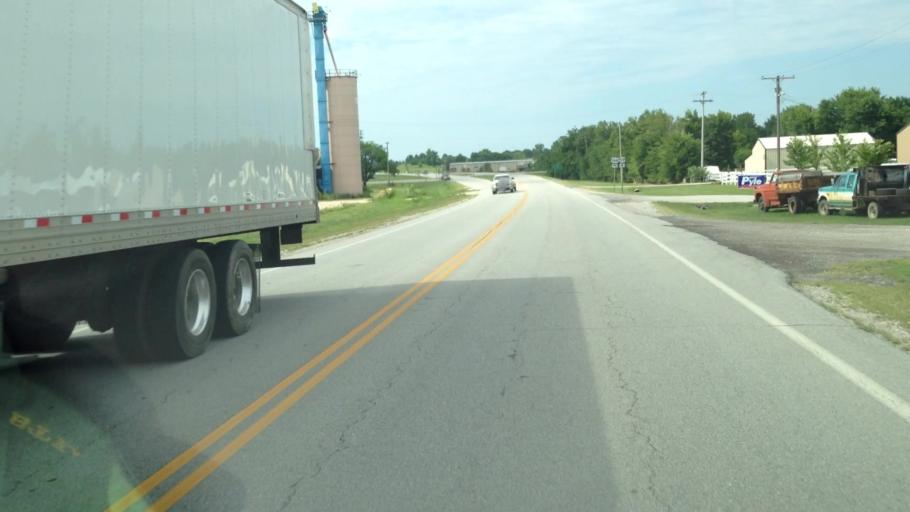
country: US
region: Kansas
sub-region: Labette County
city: Chetopa
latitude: 37.0451
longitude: -95.1001
